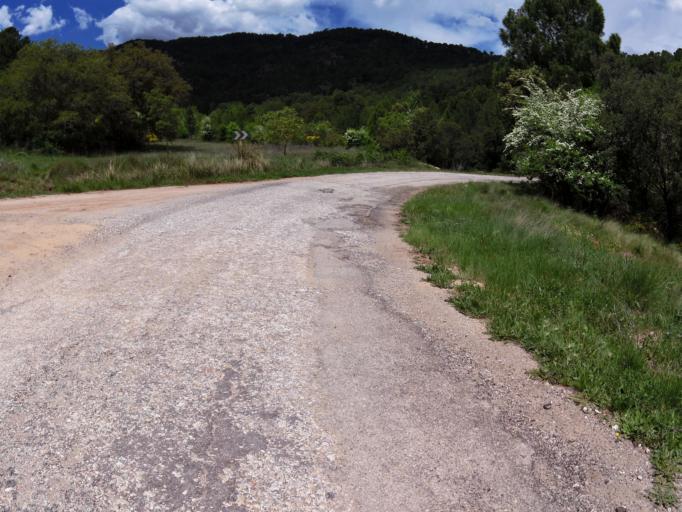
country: ES
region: Castille-La Mancha
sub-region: Provincia de Albacete
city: Paterna del Madera
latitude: 38.5784
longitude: -2.3419
